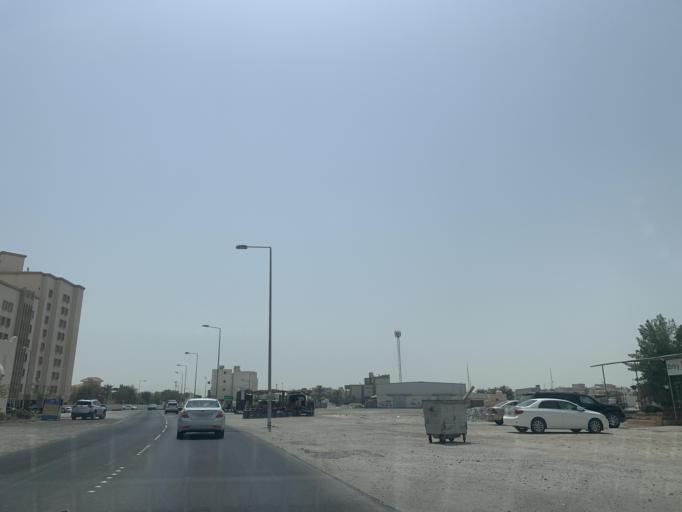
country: BH
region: Northern
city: Madinat `Isa
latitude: 26.1853
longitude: 50.5582
